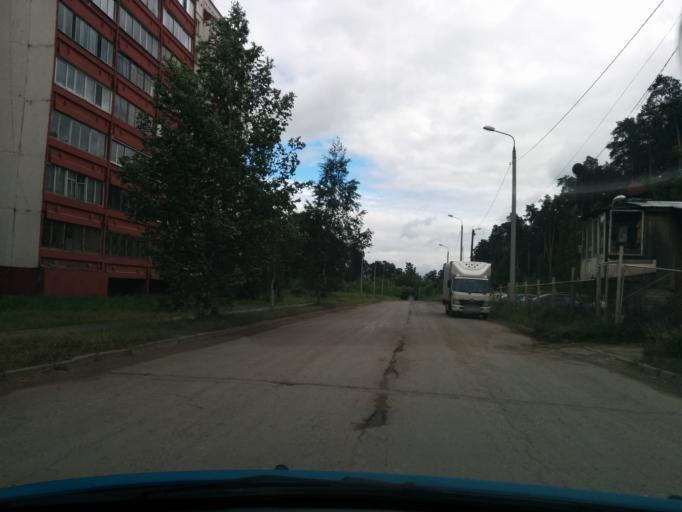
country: RU
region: Perm
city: Kondratovo
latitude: 58.0220
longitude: 56.0043
